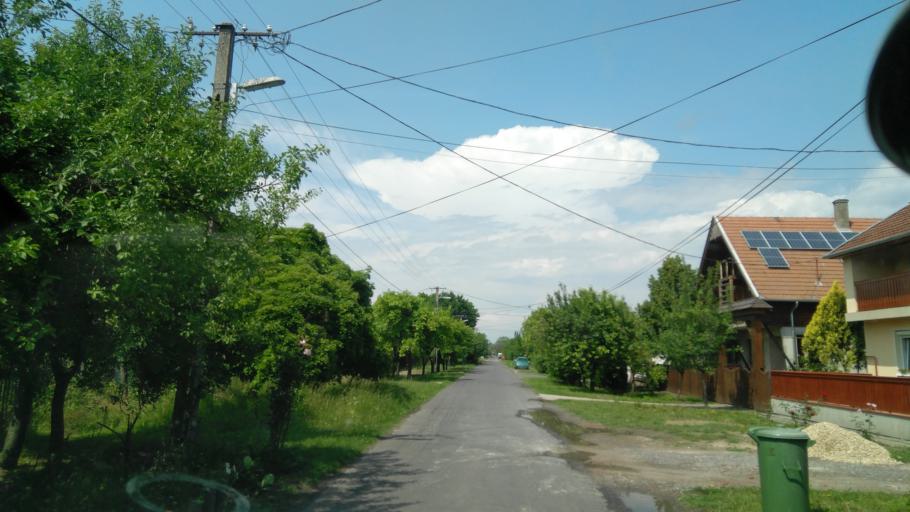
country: HU
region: Bekes
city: Bekes
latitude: 46.7567
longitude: 21.1461
